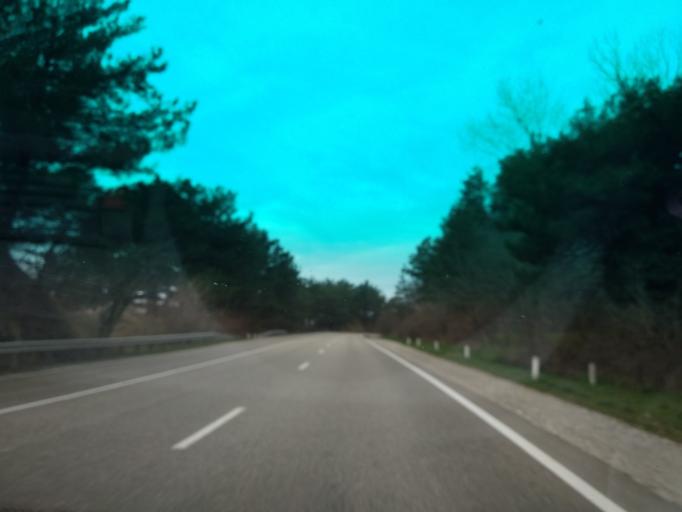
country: RU
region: Krasnodarskiy
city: Ol'ginka
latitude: 44.1862
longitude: 38.9161
